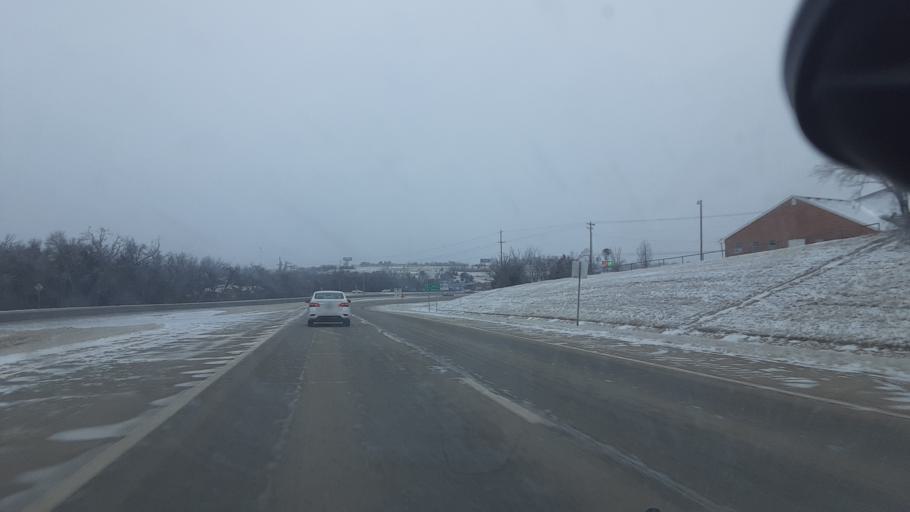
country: US
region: Oklahoma
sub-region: Logan County
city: Guthrie
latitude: 35.8809
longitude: -97.3880
